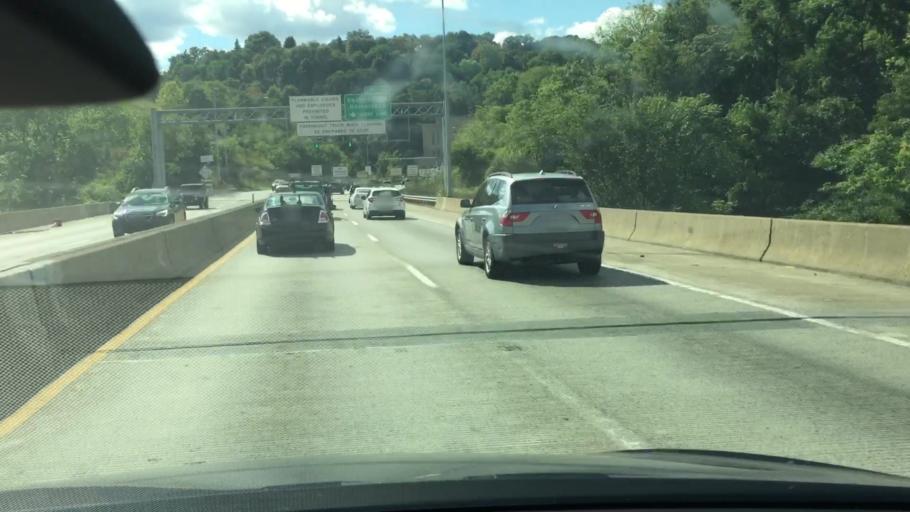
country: US
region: Pennsylvania
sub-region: Allegheny County
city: Homestead
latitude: 40.4265
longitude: -79.9068
